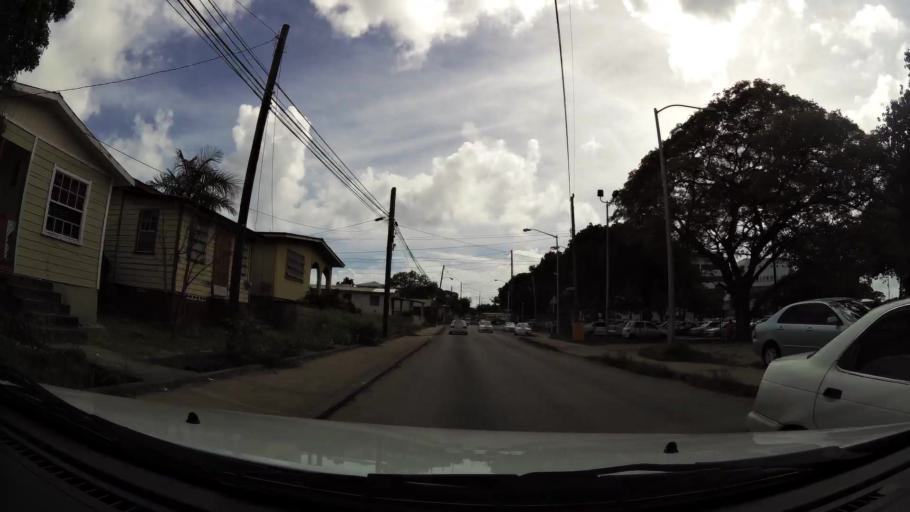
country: BB
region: Saint Michael
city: Bridgetown
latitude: 13.0969
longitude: -59.6058
